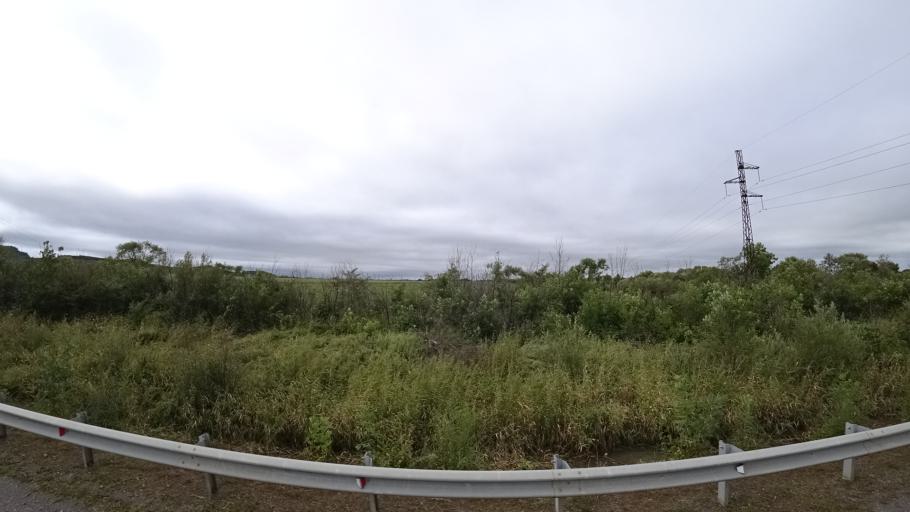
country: RU
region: Primorskiy
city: Monastyrishche
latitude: 44.1808
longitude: 132.4415
